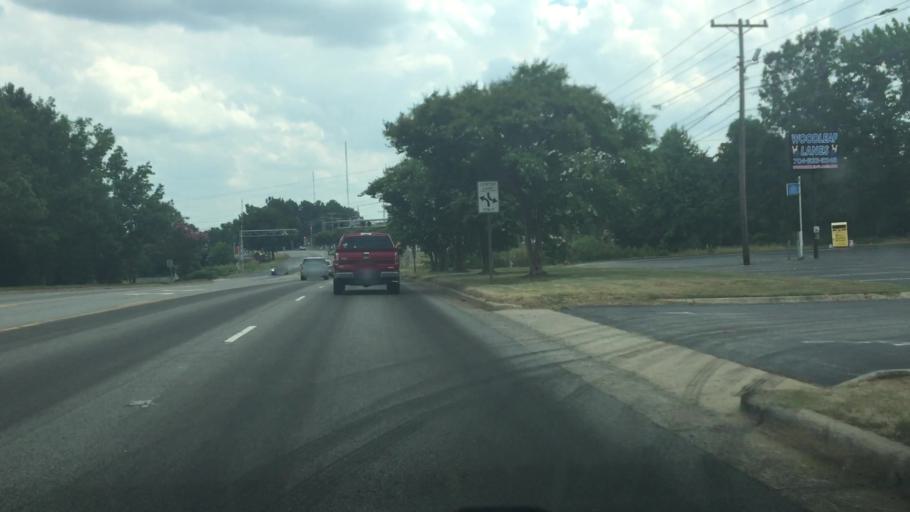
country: US
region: North Carolina
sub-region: Rowan County
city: Salisbury
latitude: 35.6853
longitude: -80.5085
